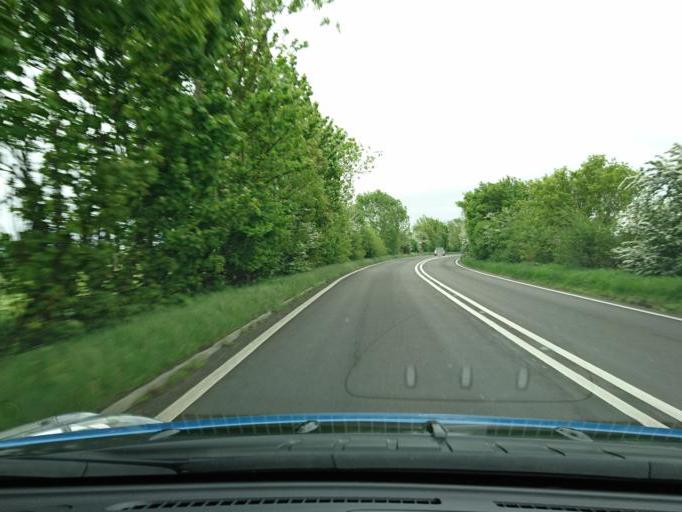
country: GB
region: England
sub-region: Oxfordshire
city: Stanford in the Vale
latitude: 51.6773
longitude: -1.4732
